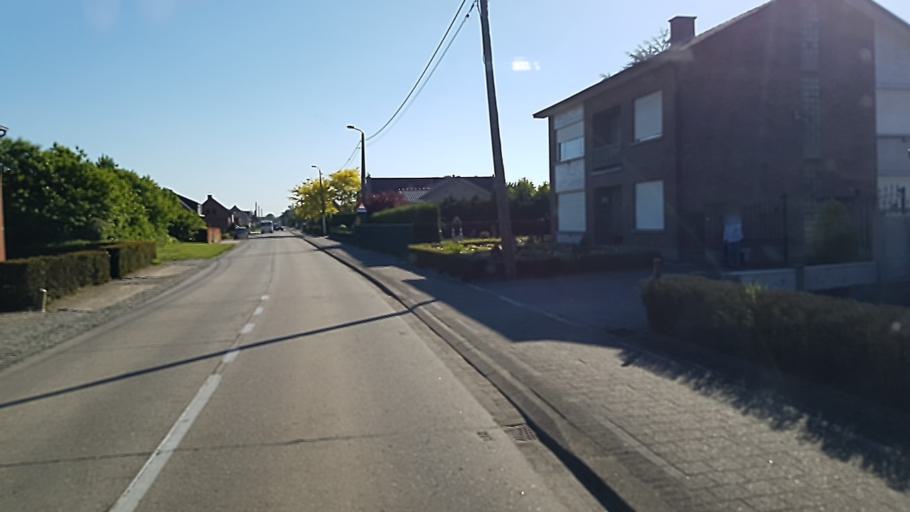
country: BE
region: Flanders
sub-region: Provincie Antwerpen
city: Berlaar
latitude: 51.0910
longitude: 4.6881
